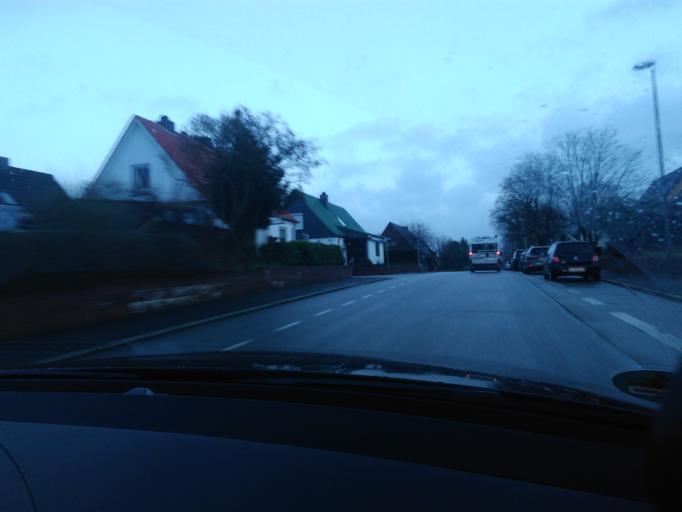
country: DE
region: Schleswig-Holstein
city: Altenholz
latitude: 54.3972
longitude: 10.1596
